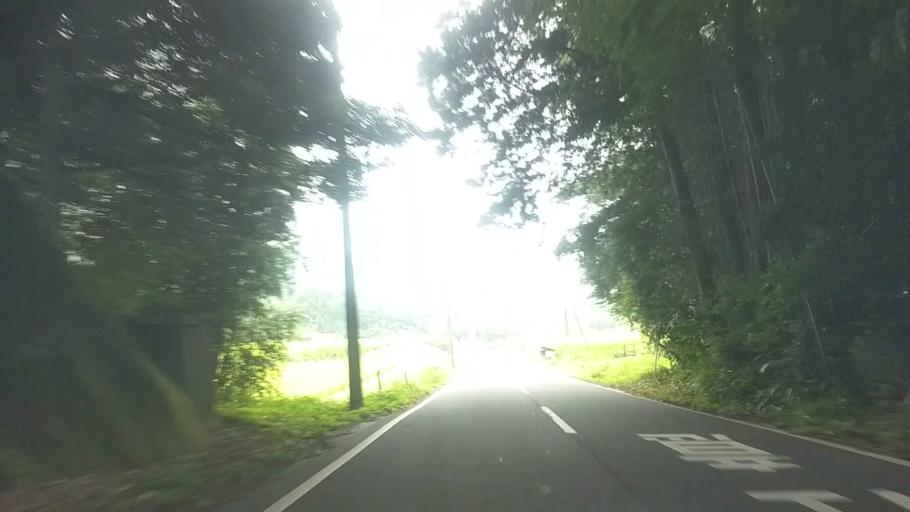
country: JP
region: Chiba
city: Kimitsu
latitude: 35.2423
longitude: 139.9960
